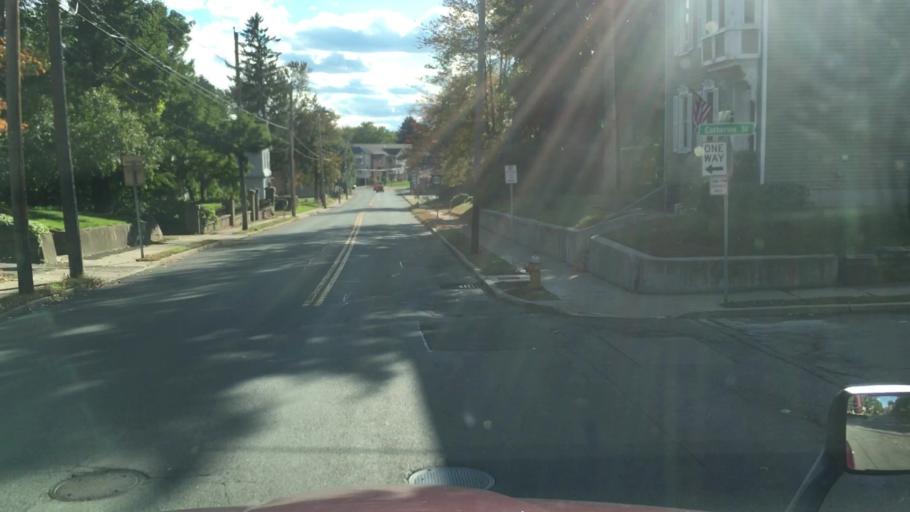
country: US
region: New York
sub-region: Schenectady County
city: Scotia
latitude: 42.8274
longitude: -73.9608
